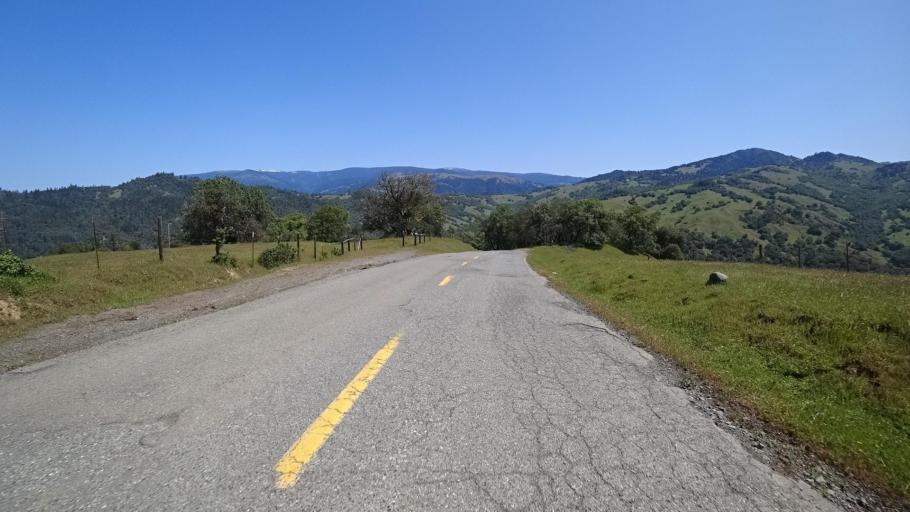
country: US
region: California
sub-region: Humboldt County
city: Redway
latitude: 40.1649
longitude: -123.6126
